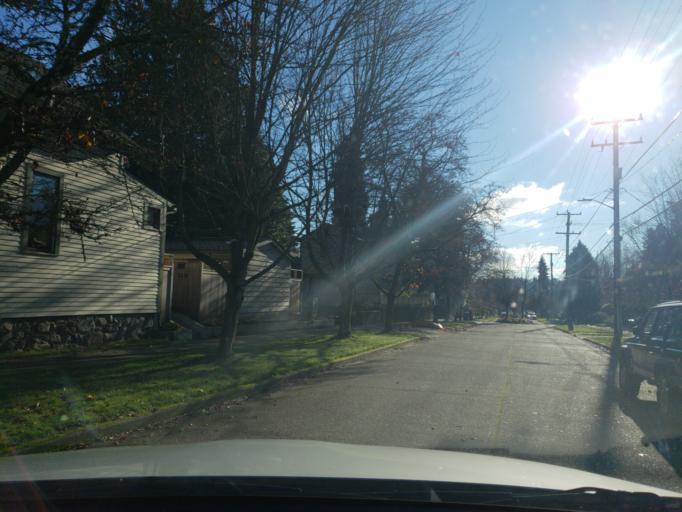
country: US
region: Washington
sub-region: King County
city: Shoreline
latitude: 47.6839
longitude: -122.3499
